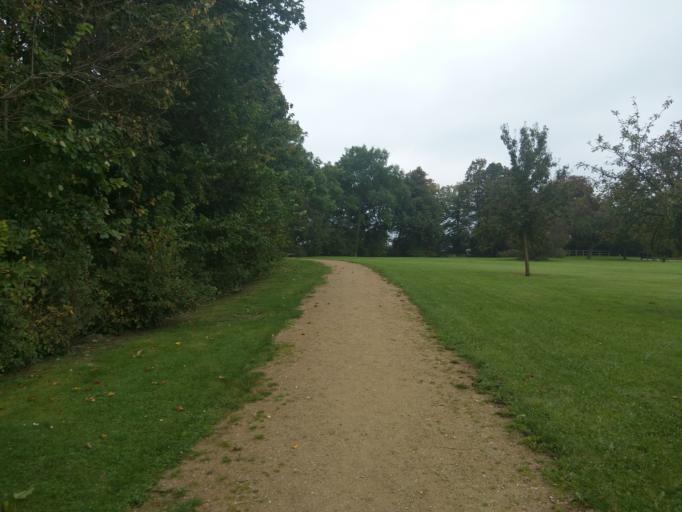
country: DE
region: Schleswig-Holstein
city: Lauenburg
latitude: 53.3727
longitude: 10.5608
